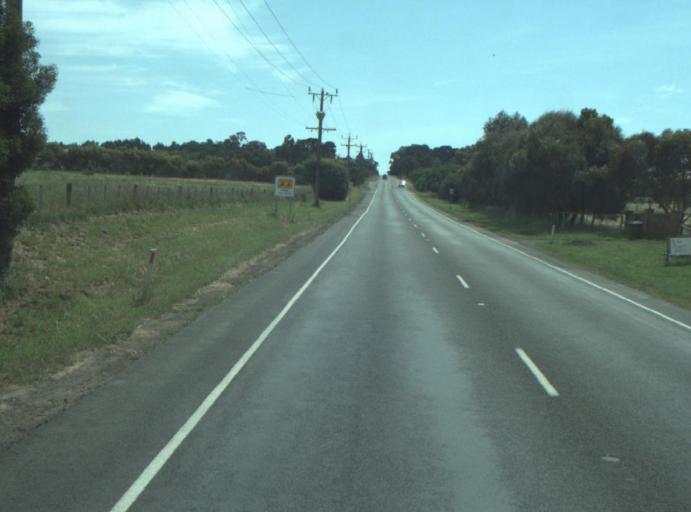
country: AU
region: Victoria
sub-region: Greater Geelong
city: Clifton Springs
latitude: -38.1570
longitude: 144.5866
